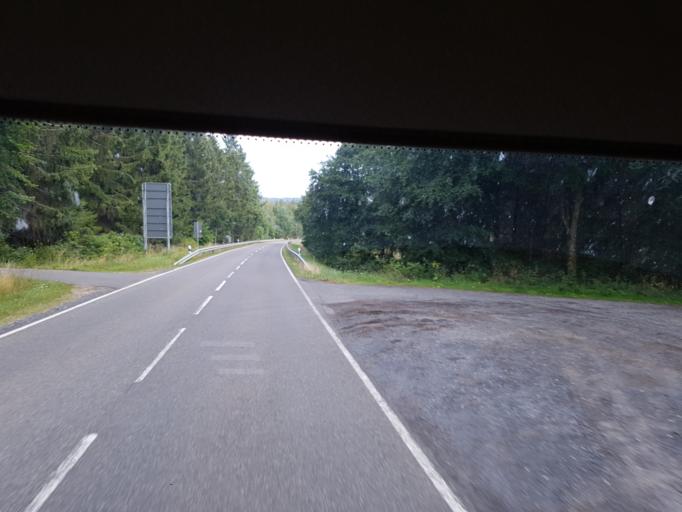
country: DE
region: Rheinland-Pfalz
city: Kradenbach
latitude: 50.2489
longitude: 6.8317
